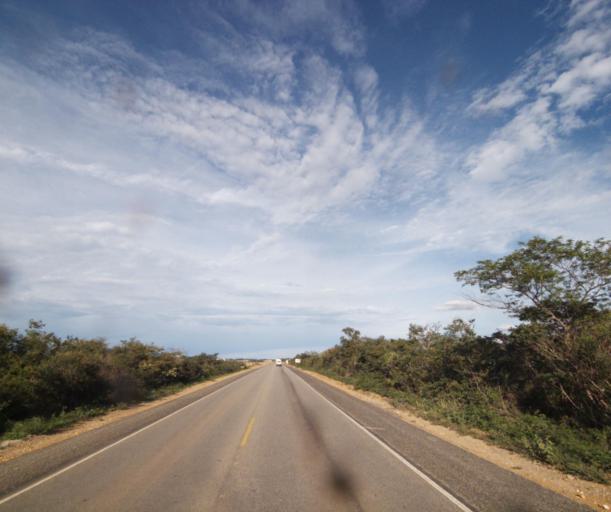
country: BR
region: Bahia
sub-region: Caetite
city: Caetite
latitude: -14.0749
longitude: -42.5453
